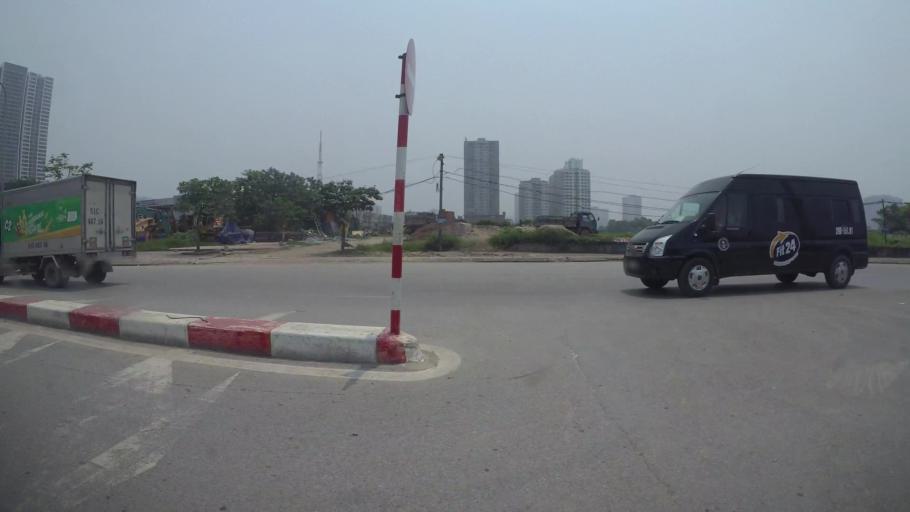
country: VN
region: Ha Noi
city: Thanh Xuan
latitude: 20.9980
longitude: 105.7802
